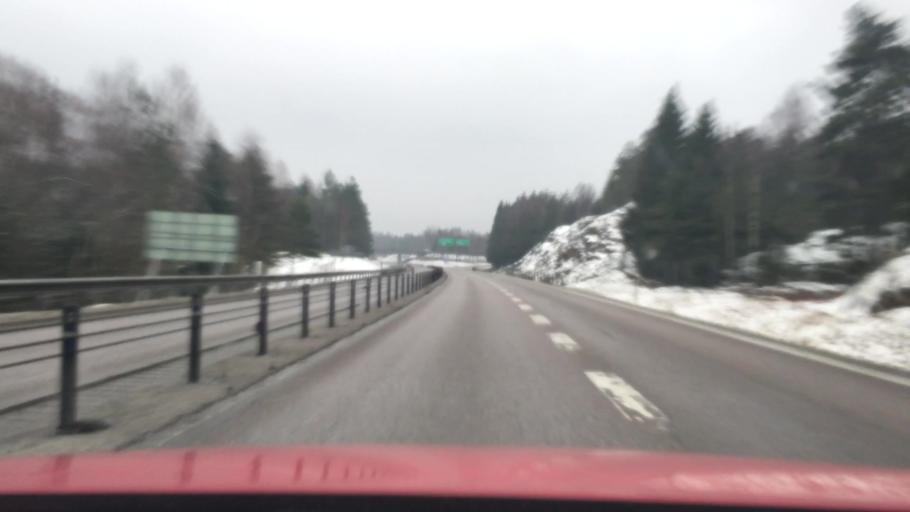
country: SE
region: Vaestra Goetaland
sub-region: Vanersborgs Kommun
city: Vanersborg
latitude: 58.3389
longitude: 12.3009
